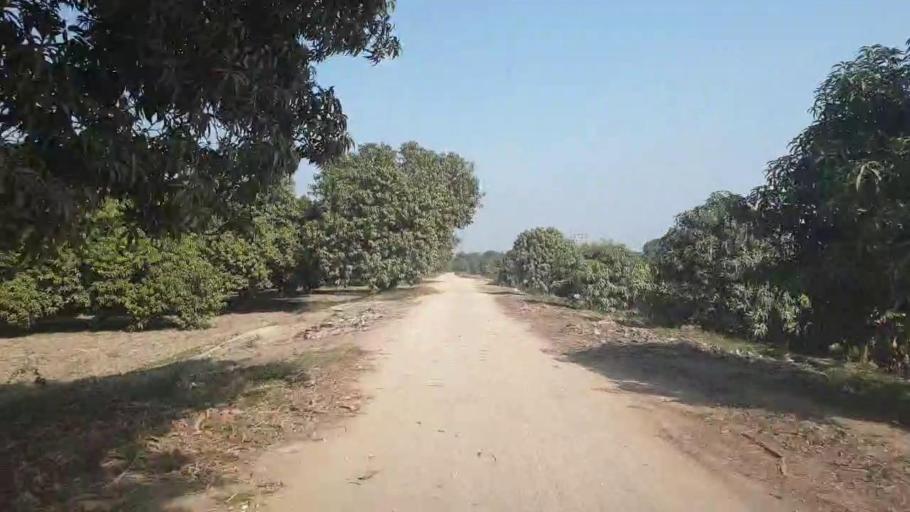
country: PK
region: Sindh
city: Tando Allahyar
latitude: 25.4680
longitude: 68.7820
